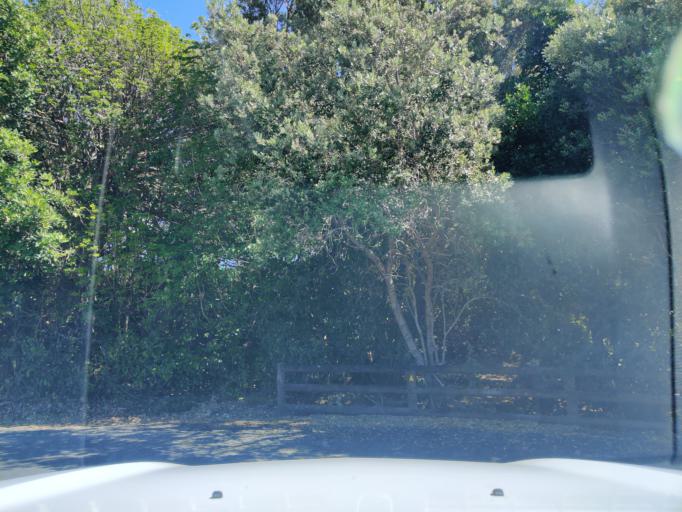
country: NZ
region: Waikato
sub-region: Thames-Coromandel District
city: Thames
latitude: -37.0384
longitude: 175.2945
